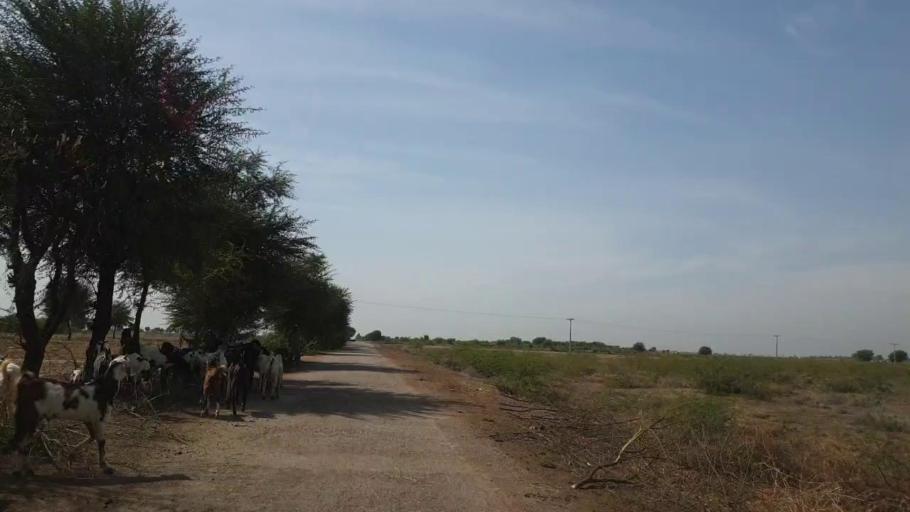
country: PK
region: Sindh
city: Kunri
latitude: 25.2124
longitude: 69.5434
